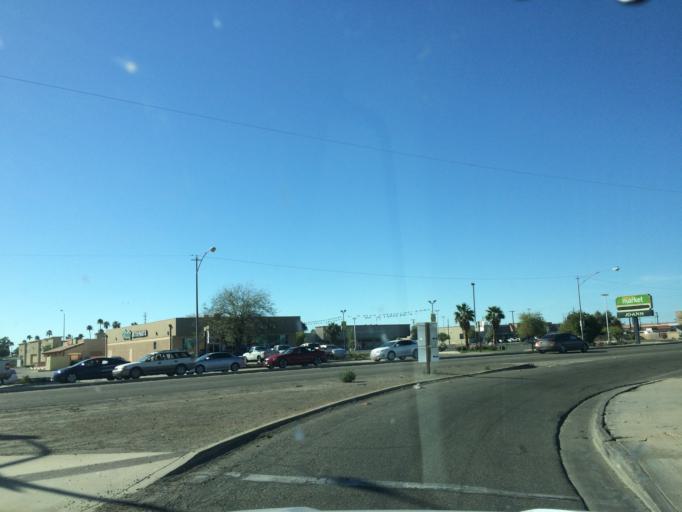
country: US
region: California
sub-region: Imperial County
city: El Centro
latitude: 32.7967
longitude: -115.5697
